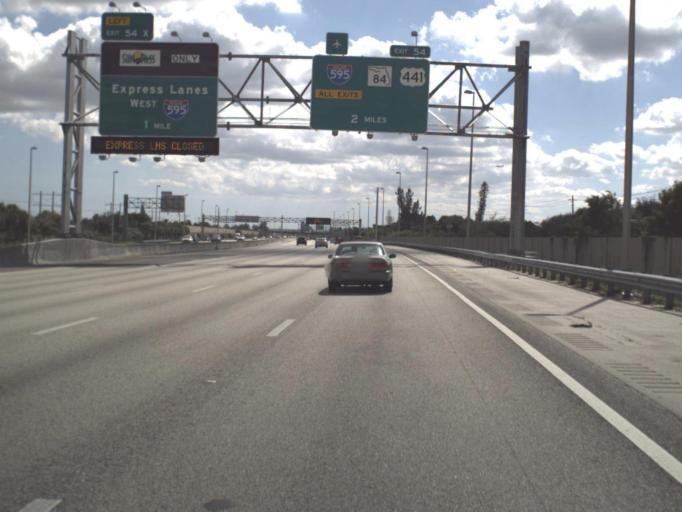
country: US
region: Florida
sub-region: Broward County
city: Broadview Park
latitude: 26.1174
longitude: -80.2188
